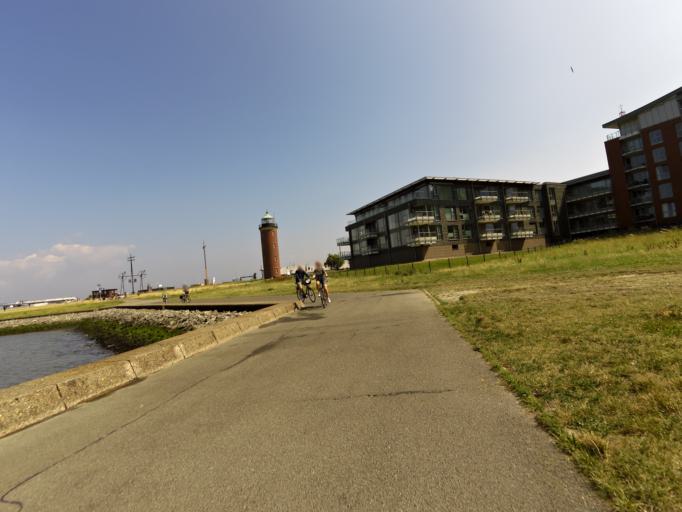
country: DE
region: Lower Saxony
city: Cuxhaven
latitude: 53.8726
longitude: 8.7067
